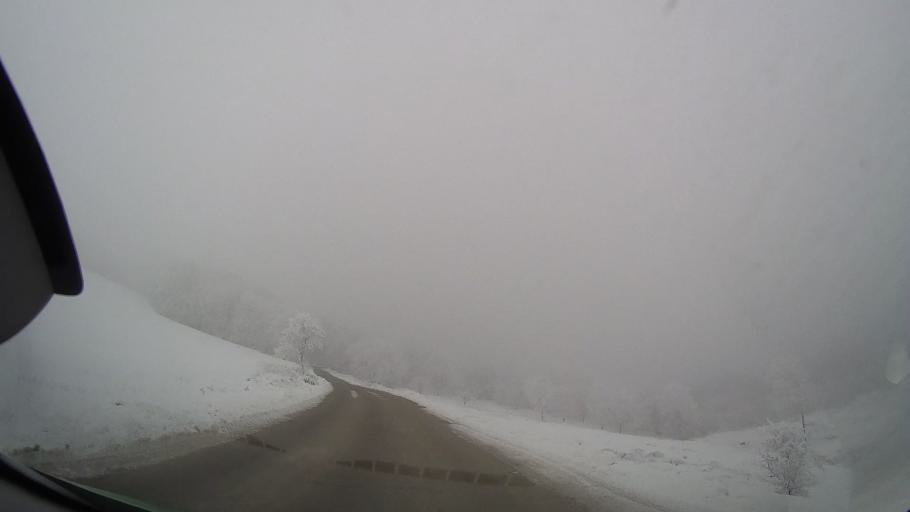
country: RO
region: Neamt
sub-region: Comuna Valea Ursului
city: Valea Ursului
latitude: 46.8361
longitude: 27.0710
